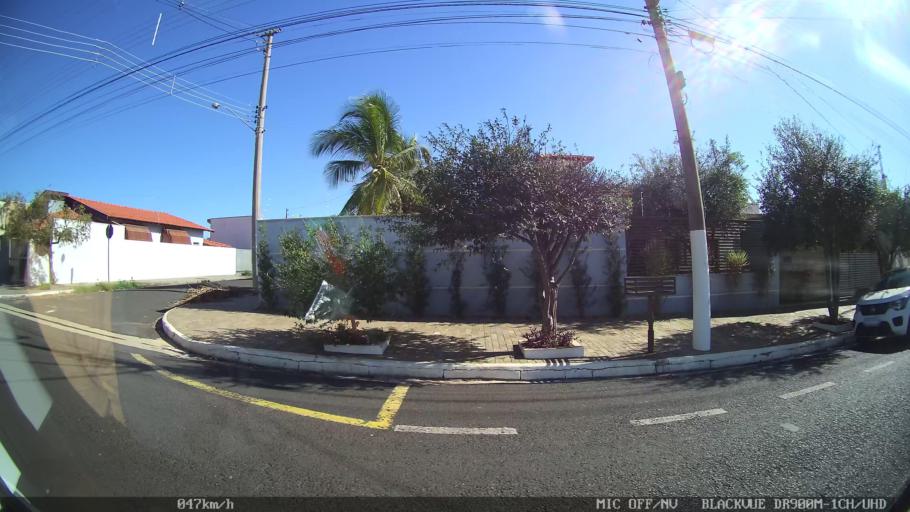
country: BR
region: Sao Paulo
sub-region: Olimpia
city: Olimpia
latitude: -20.7519
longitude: -48.9129
